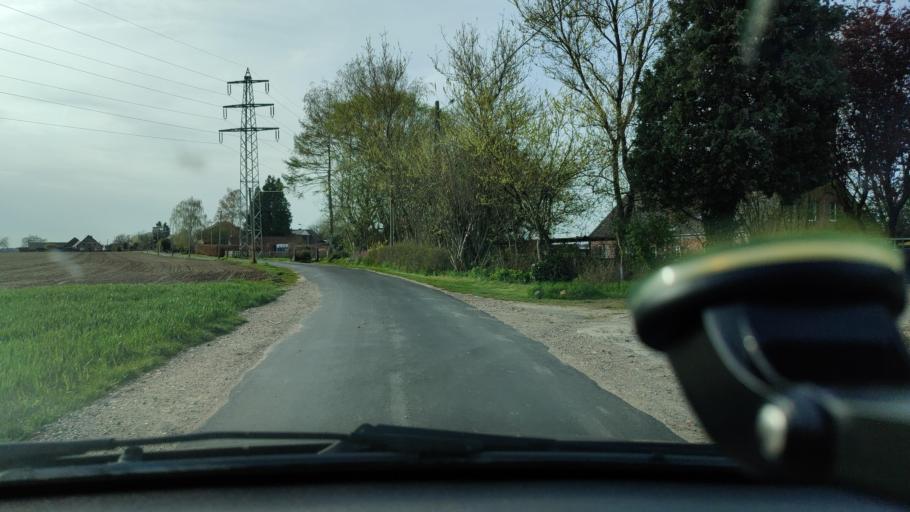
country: DE
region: North Rhine-Westphalia
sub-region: Regierungsbezirk Dusseldorf
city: Goch
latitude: 51.7401
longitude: 6.1907
